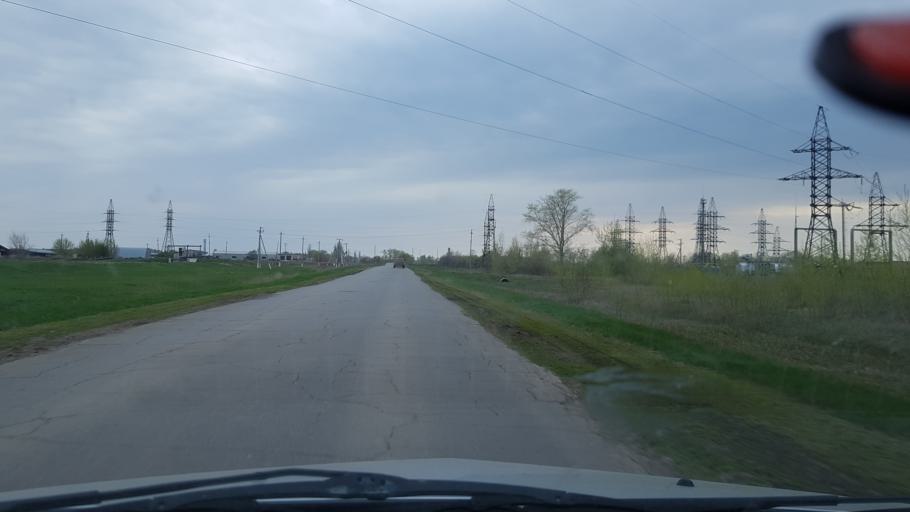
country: RU
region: Samara
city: Khryashchevka
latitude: 53.6721
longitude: 49.0901
